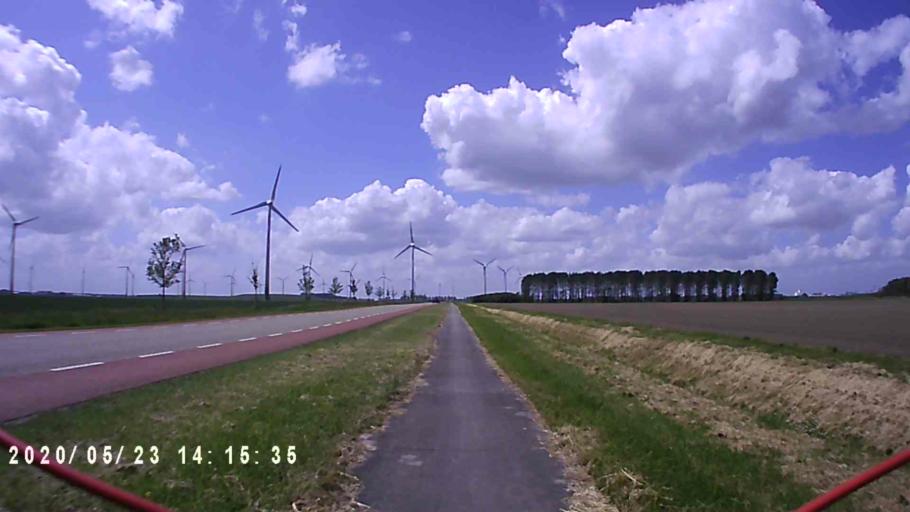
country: NL
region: Groningen
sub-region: Gemeente Delfzijl
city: Delfzijl
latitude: 53.2870
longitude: 7.0017
